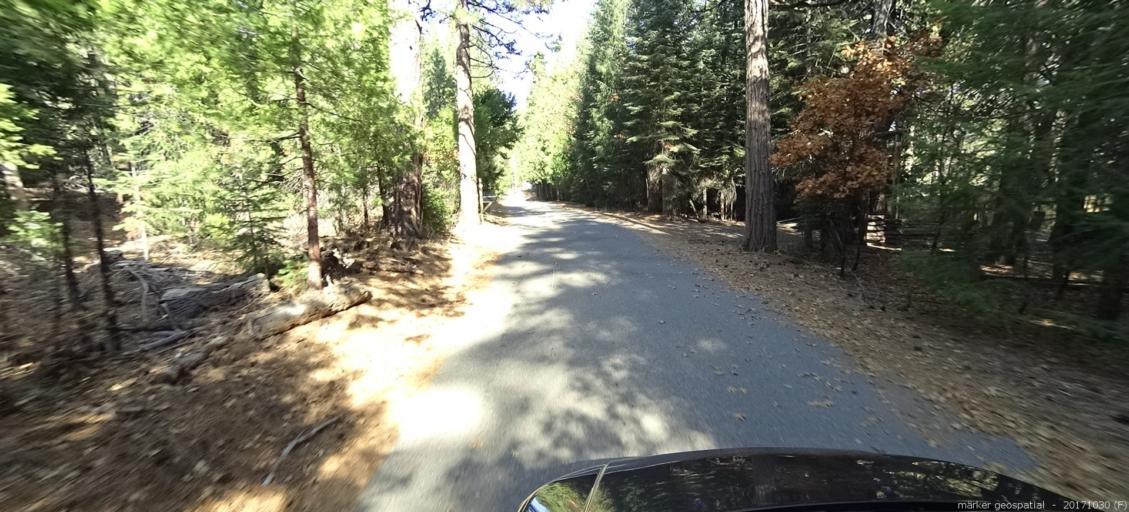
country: US
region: California
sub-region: Shasta County
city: Shingletown
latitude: 40.5055
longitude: -121.7400
